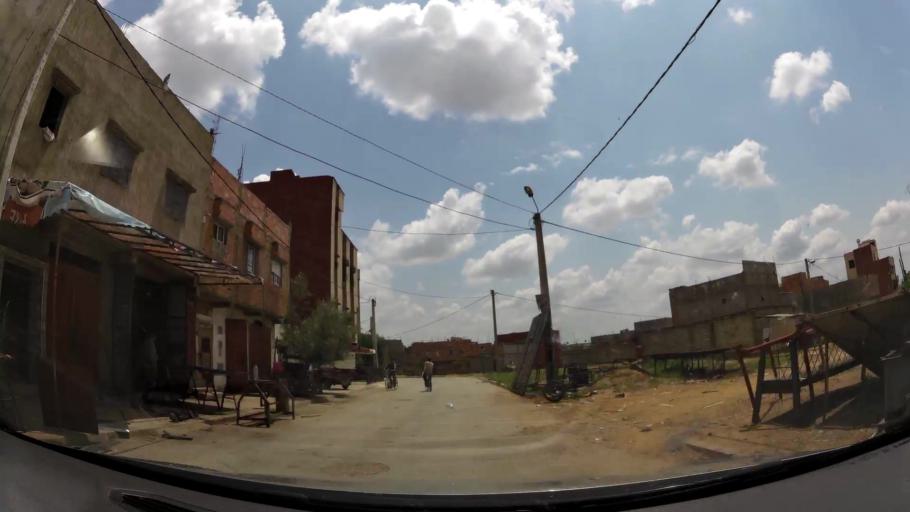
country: MA
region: Rabat-Sale-Zemmour-Zaer
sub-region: Khemisset
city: Tiflet
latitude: 34.0004
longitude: -6.5310
